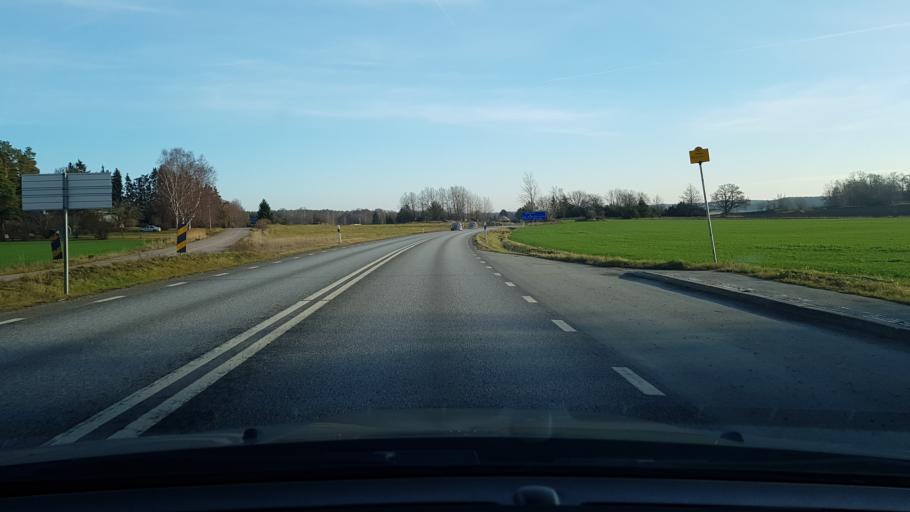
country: SE
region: Stockholm
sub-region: Vallentuna Kommun
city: Vallentuna
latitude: 59.7535
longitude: 18.0365
